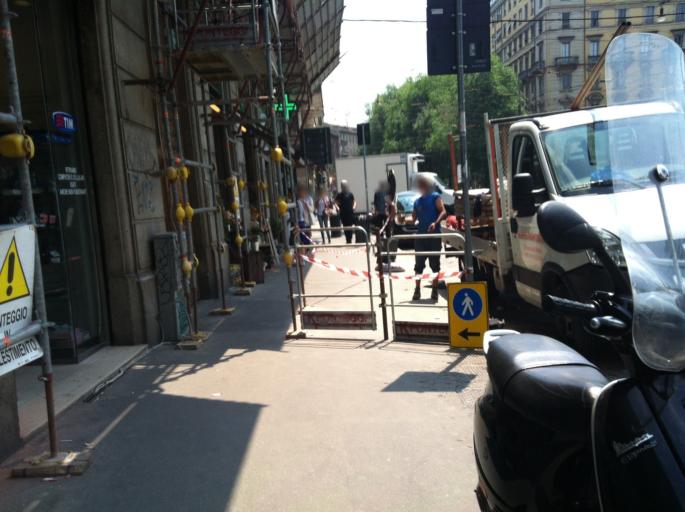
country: IT
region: Lombardy
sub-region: Citta metropolitana di Milano
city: Milano
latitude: 45.4624
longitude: 9.2075
